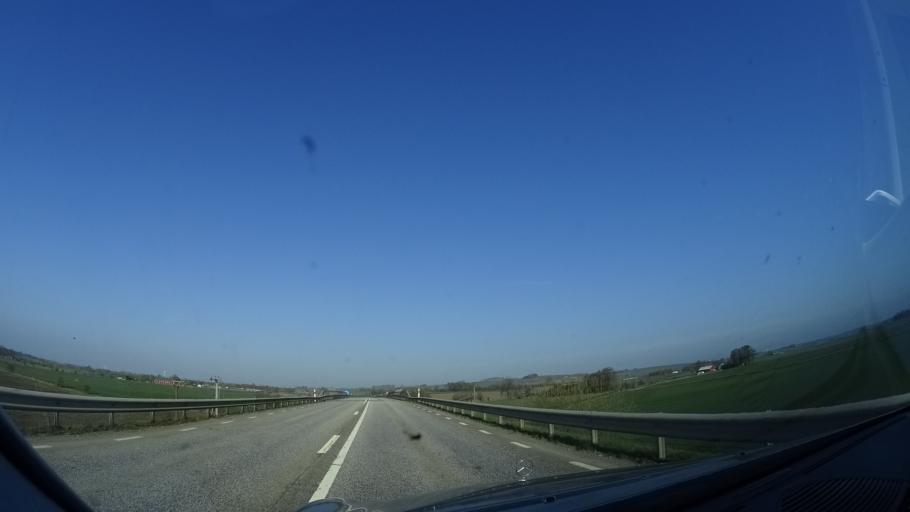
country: SE
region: Skane
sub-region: Landskrona
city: Asmundtorp
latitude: 55.8905
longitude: 12.9843
